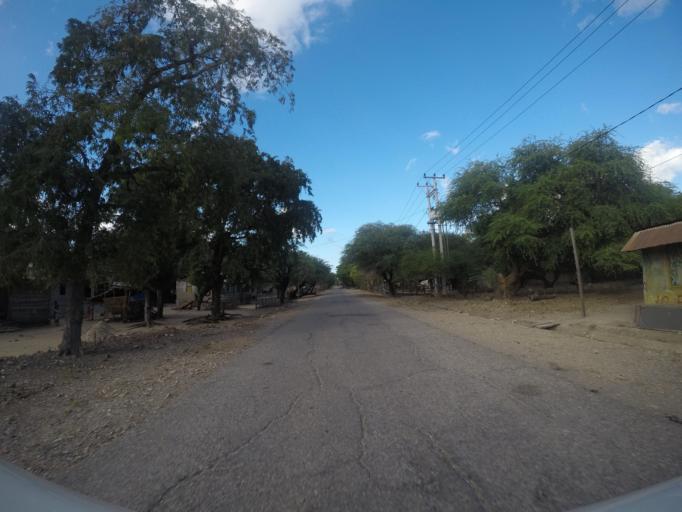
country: TL
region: Lautem
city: Lospalos
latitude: -8.3556
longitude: 126.9124
